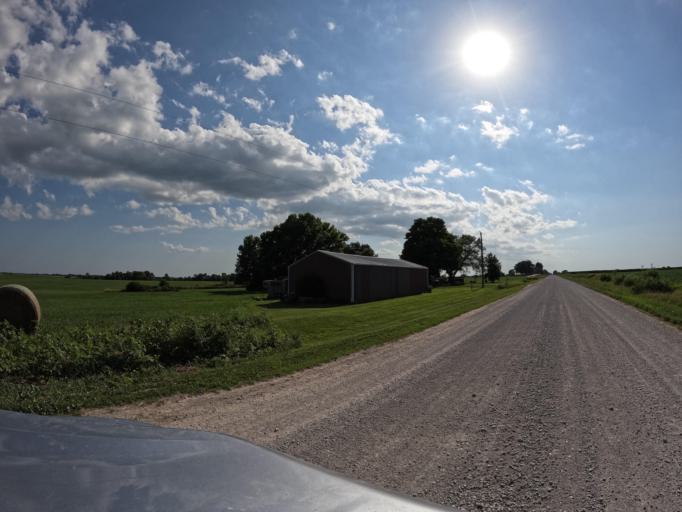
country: US
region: Iowa
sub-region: Appanoose County
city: Centerville
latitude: 40.7179
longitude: -93.0031
